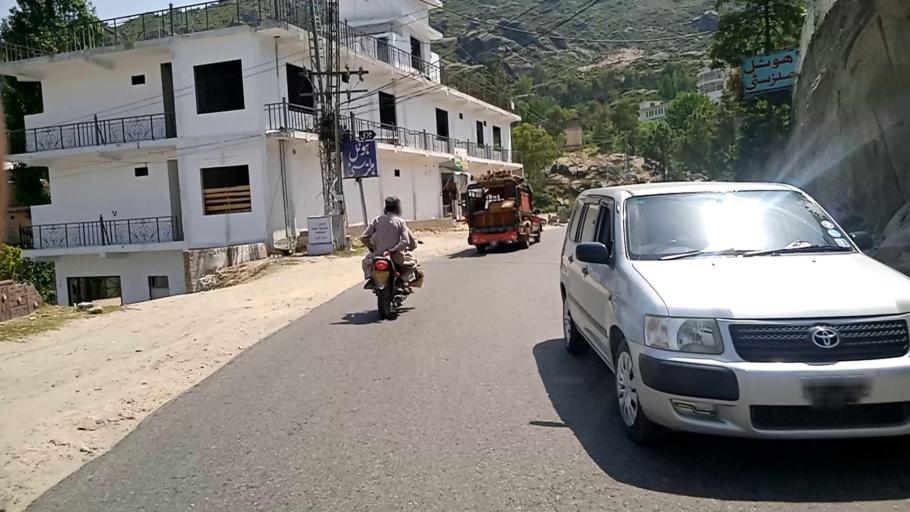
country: PK
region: Khyber Pakhtunkhwa
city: Mingora
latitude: 34.7932
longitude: 72.3952
